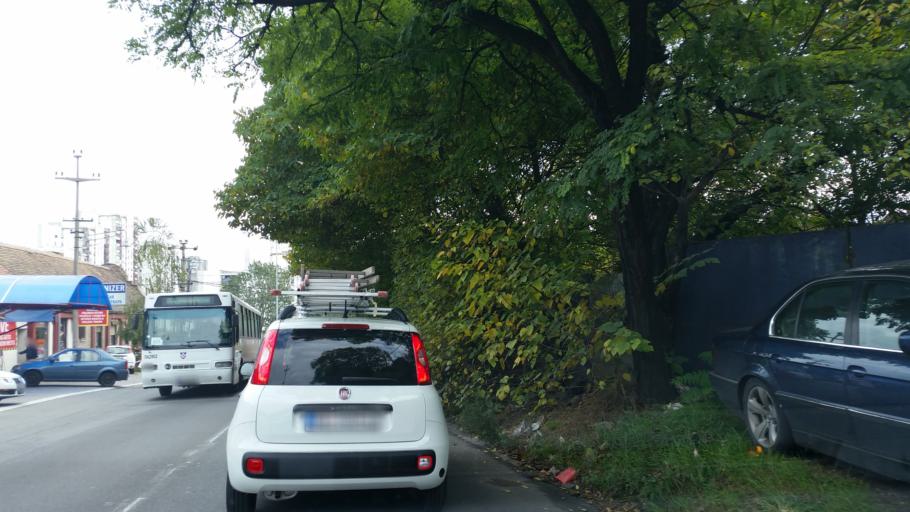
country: RS
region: Central Serbia
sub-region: Belgrade
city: Zemun
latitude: 44.8044
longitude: 20.3658
